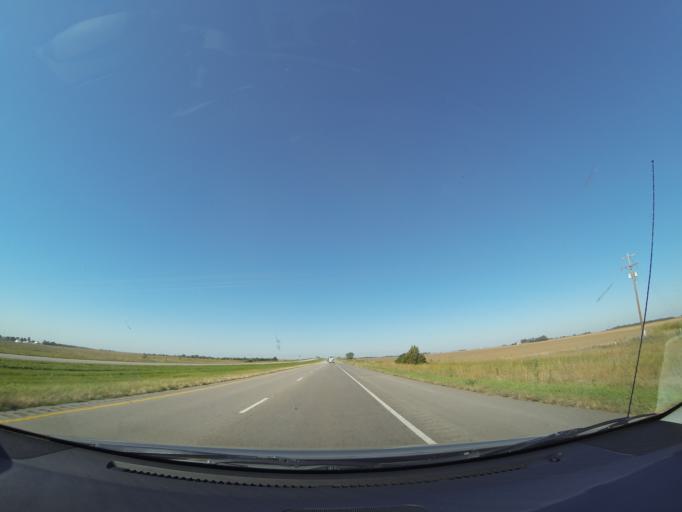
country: US
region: Nebraska
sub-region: Seward County
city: Seward
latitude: 40.8227
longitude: -97.2347
